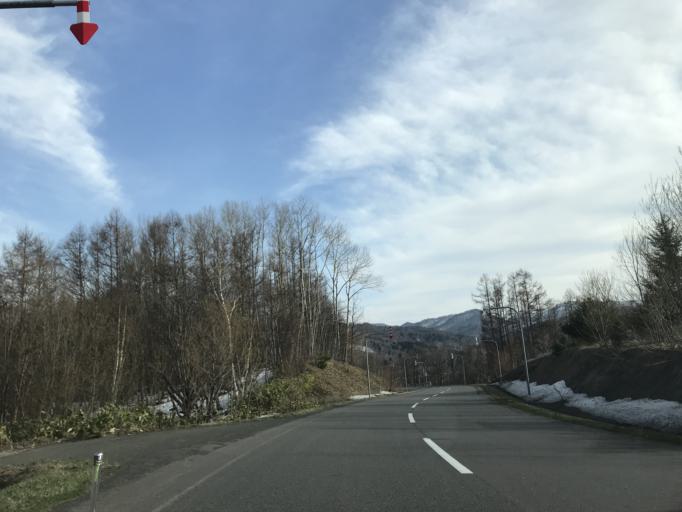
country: JP
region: Hokkaido
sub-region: Asahikawa-shi
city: Asahikawa
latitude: 43.6969
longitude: 142.3304
